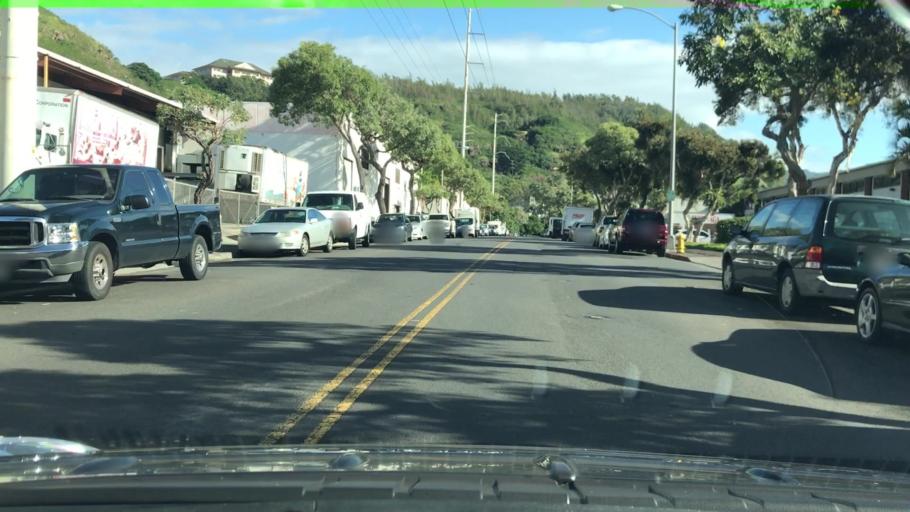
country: US
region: Hawaii
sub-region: Honolulu County
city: Halawa Heights
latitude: 21.3779
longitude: -157.9098
